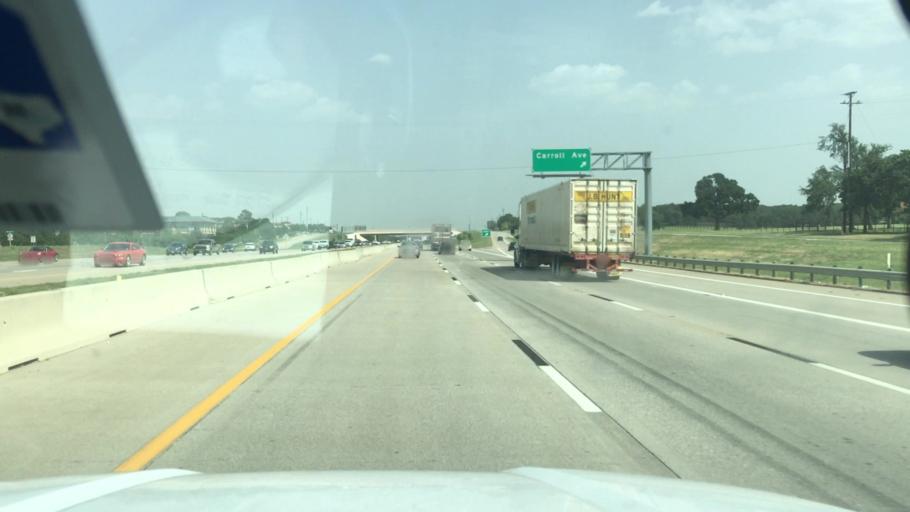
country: US
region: Texas
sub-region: Tarrant County
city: Southlake
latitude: 32.9564
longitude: -97.1406
